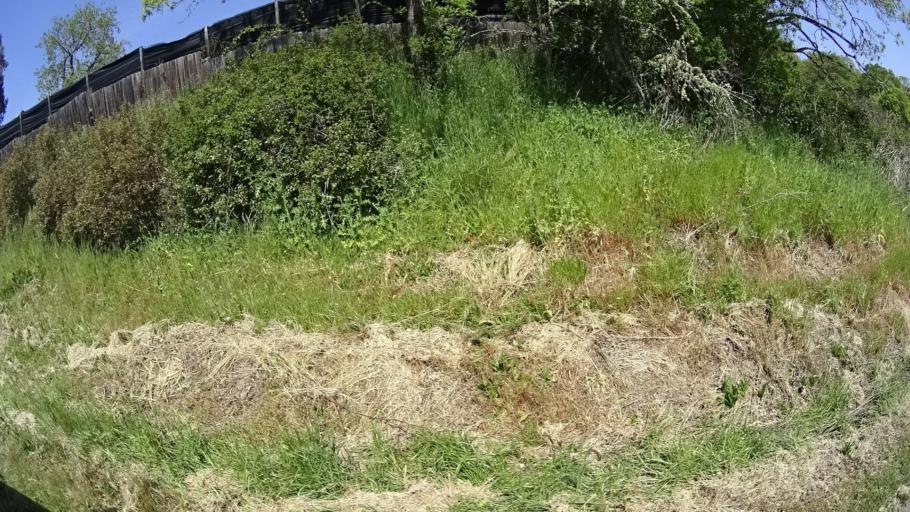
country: US
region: California
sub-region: Humboldt County
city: Redway
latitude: 40.2749
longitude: -123.6352
